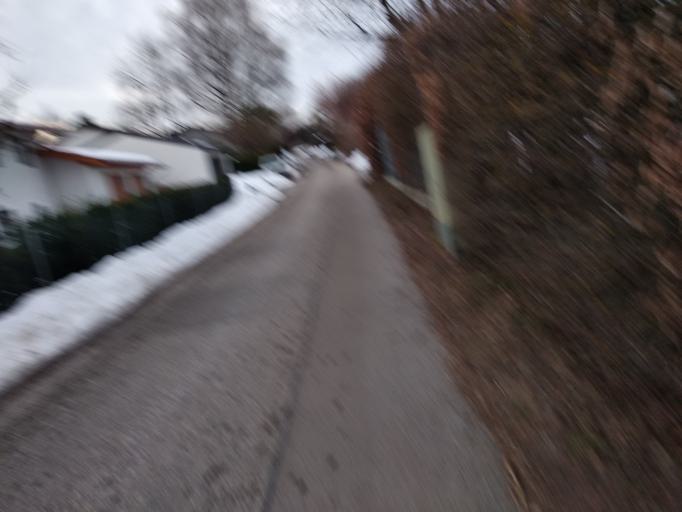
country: DE
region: Bavaria
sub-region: Upper Bavaria
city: Ebersberg
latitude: 48.0825
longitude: 11.9778
